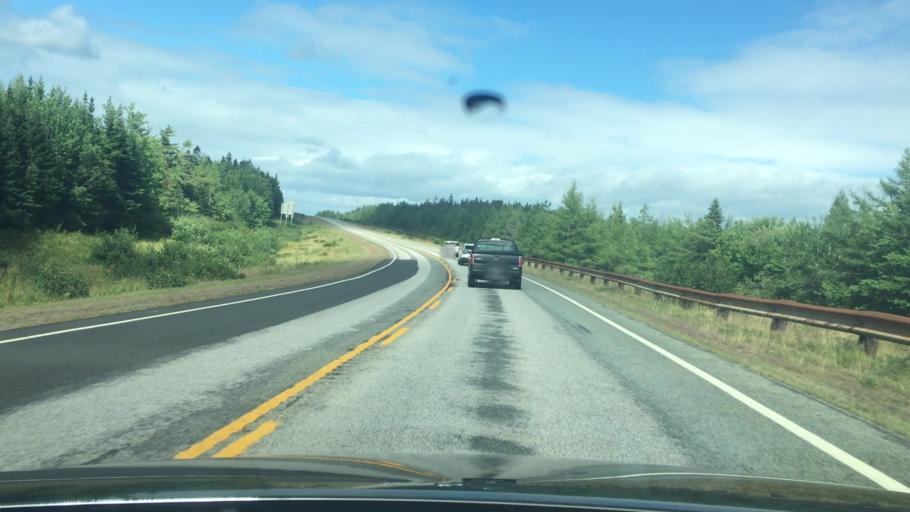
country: CA
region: Nova Scotia
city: Princeville
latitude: 45.6135
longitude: -61.0569
